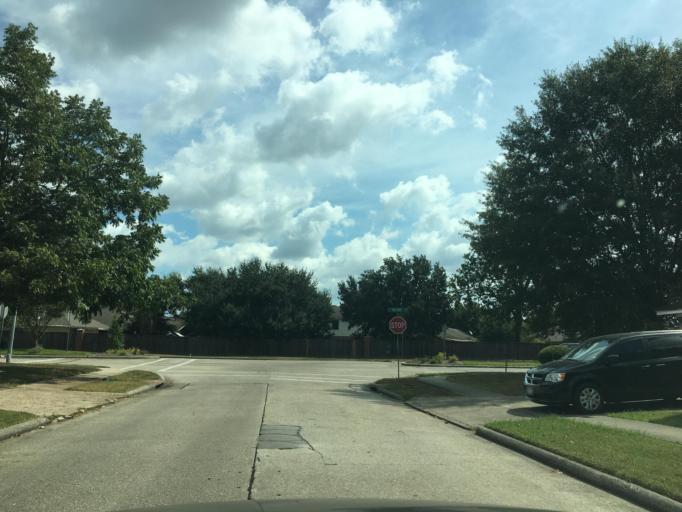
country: US
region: Texas
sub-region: Harris County
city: Spring
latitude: 30.1147
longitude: -95.3954
